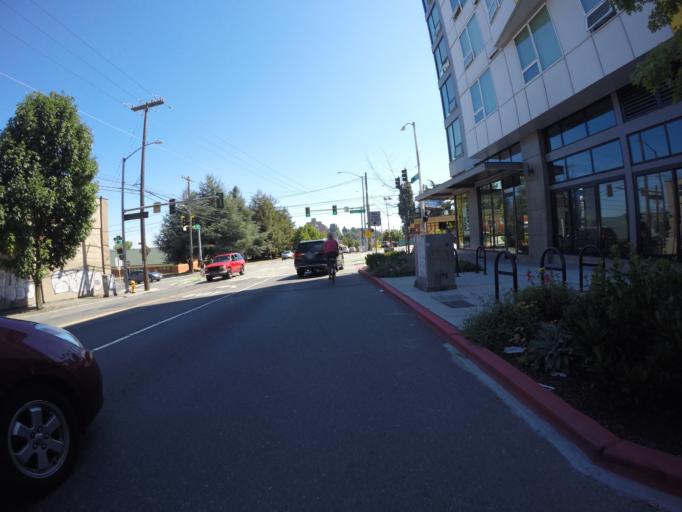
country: US
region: Washington
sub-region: King County
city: Seattle
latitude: 47.6019
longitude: -122.3169
